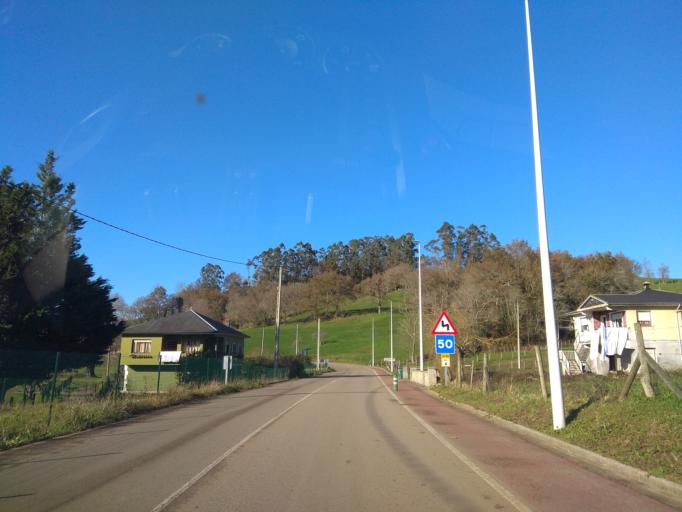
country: ES
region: Cantabria
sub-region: Provincia de Cantabria
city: Entrambasaguas
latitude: 43.3726
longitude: -3.6627
